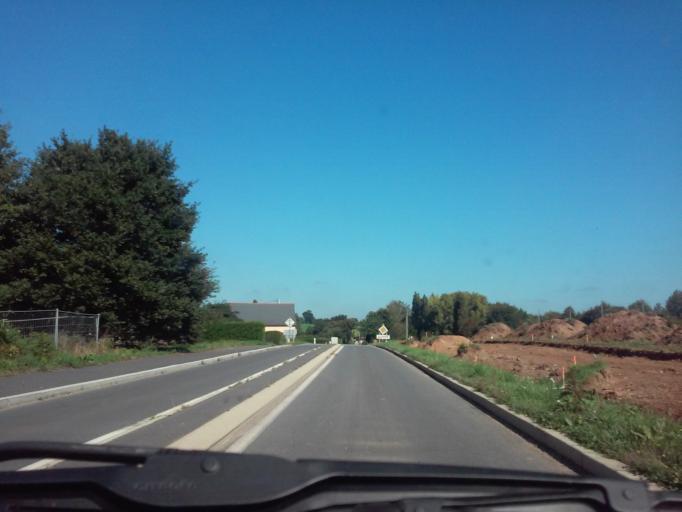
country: FR
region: Brittany
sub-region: Departement d'Ille-et-Vilaine
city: Chevaigne
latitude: 48.1940
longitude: -1.6251
